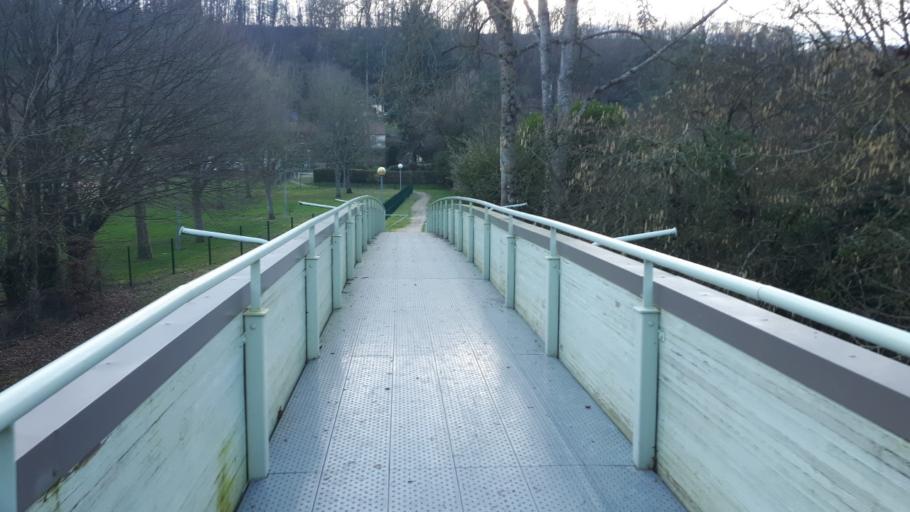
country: FR
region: Centre
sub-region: Departement du Loir-et-Cher
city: Montoire-sur-le-Loir
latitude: 47.7495
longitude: 0.8626
